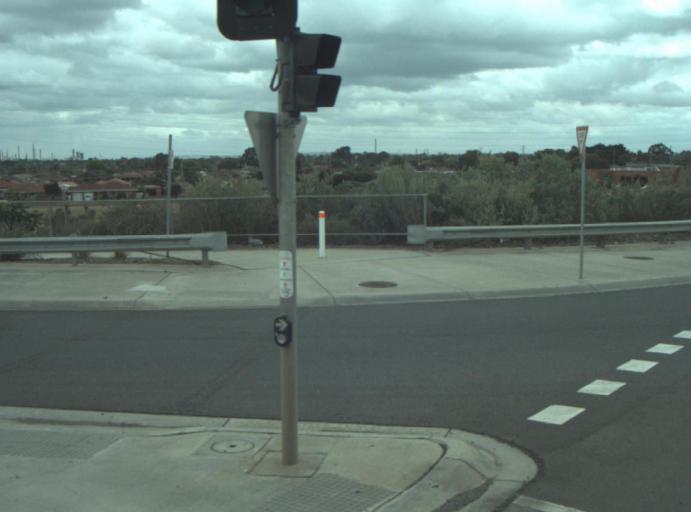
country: AU
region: Victoria
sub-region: Greater Geelong
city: Bell Post Hill
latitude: -38.0787
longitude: 144.3351
